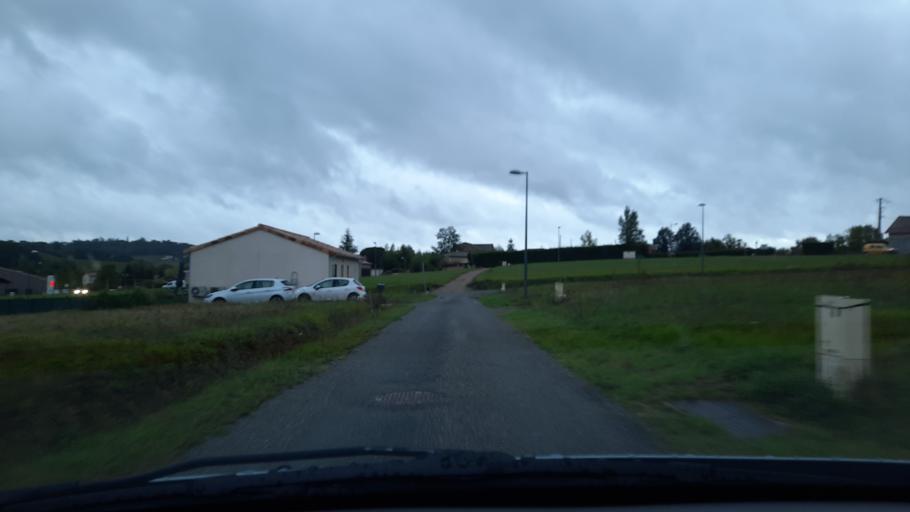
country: FR
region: Midi-Pyrenees
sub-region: Departement du Tarn-et-Garonne
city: Molieres
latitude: 44.1940
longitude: 1.2862
